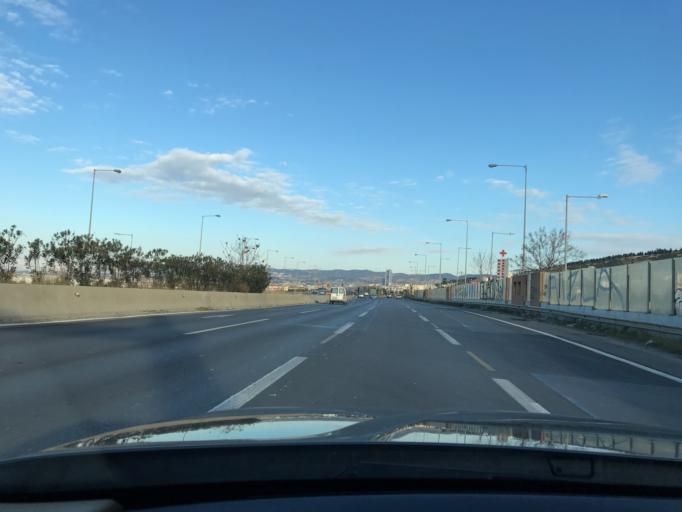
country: GR
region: Central Macedonia
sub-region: Nomos Thessalonikis
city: Polichni
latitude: 40.6747
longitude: 22.9604
